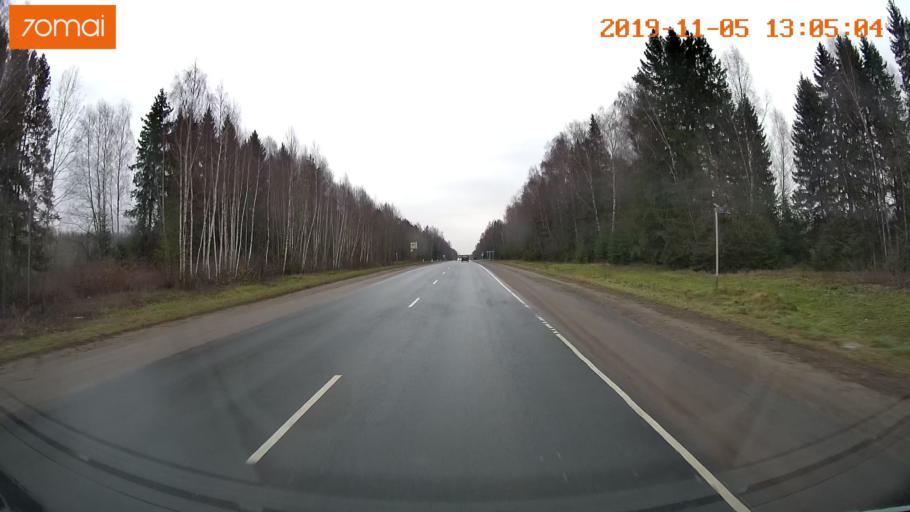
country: RU
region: Ivanovo
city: Kitovo
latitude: 56.8850
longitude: 41.2347
